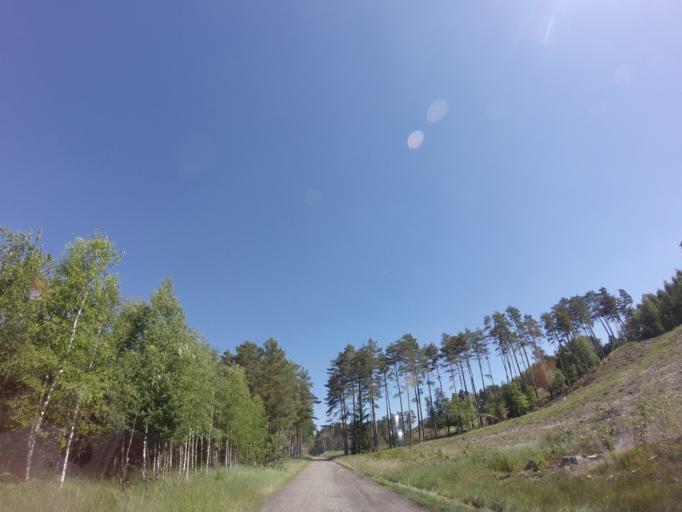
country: PL
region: West Pomeranian Voivodeship
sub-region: Powiat walecki
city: Czlopa
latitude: 53.1409
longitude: 15.9674
